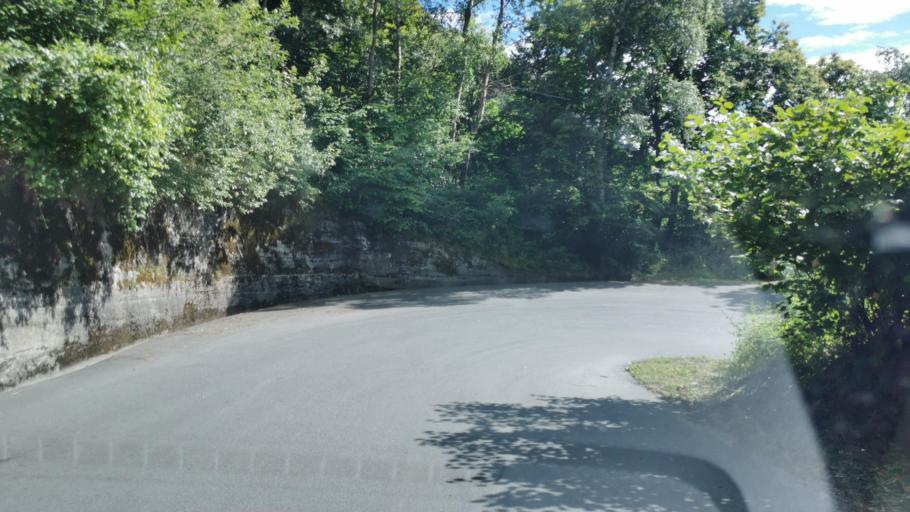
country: IT
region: Lombardy
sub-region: Provincia di Lecco
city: Casargo
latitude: 46.0378
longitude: 9.3958
